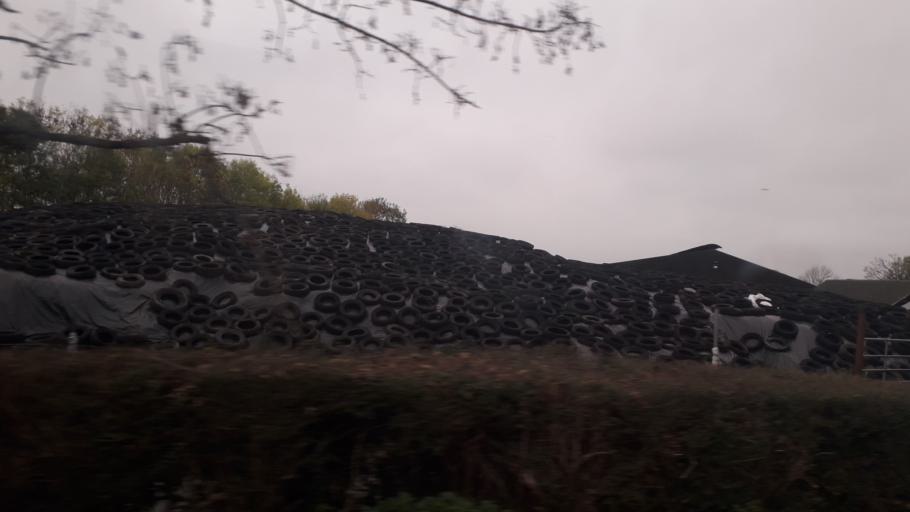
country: IE
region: Leinster
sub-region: Uibh Fhaili
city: Birr
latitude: 52.9677
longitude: -8.0052
